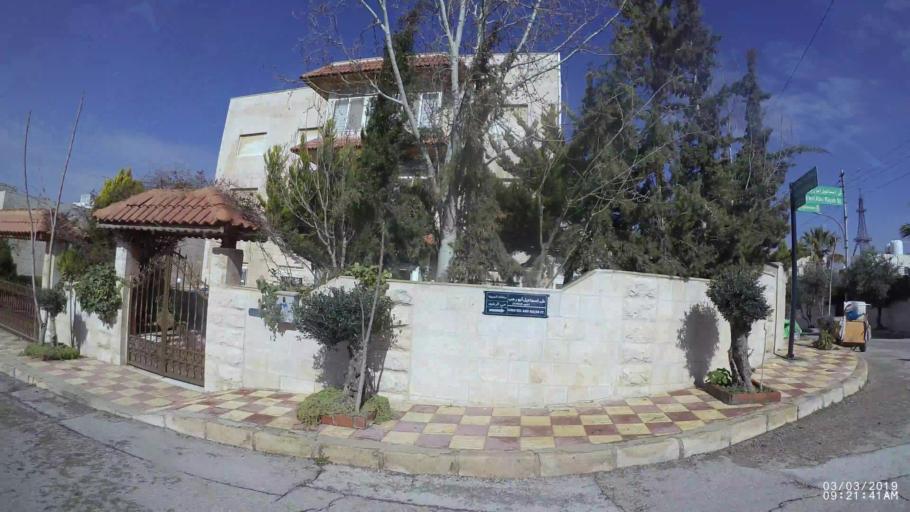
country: JO
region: Amman
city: Al Jubayhah
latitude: 32.0027
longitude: 35.8853
